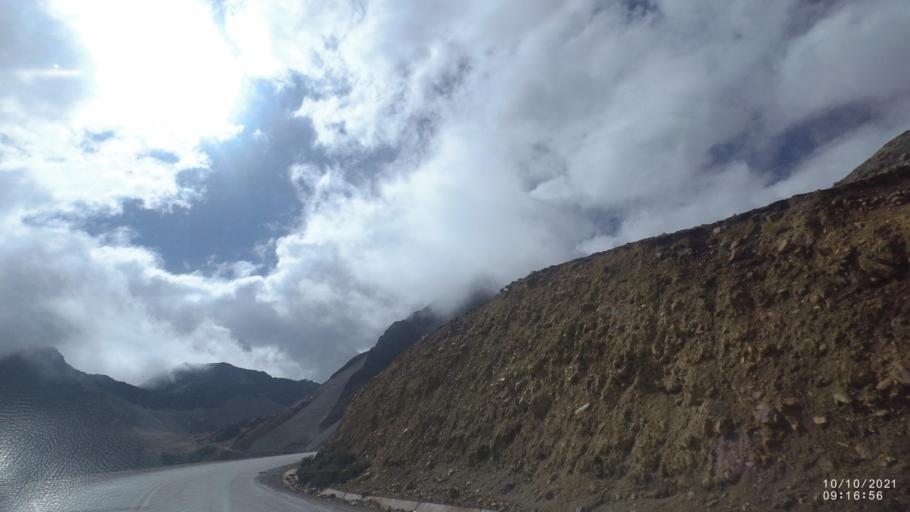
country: BO
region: La Paz
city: Quime
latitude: -17.0473
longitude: -67.2968
